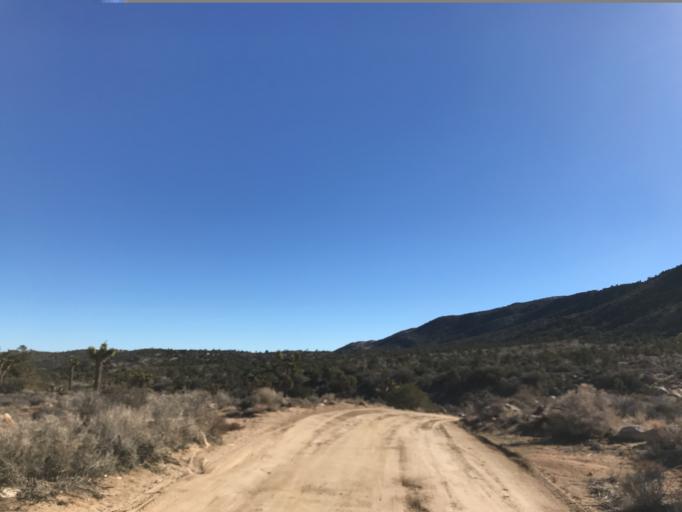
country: US
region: California
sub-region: San Bernardino County
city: Morongo Valley
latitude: 34.2237
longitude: -116.6210
